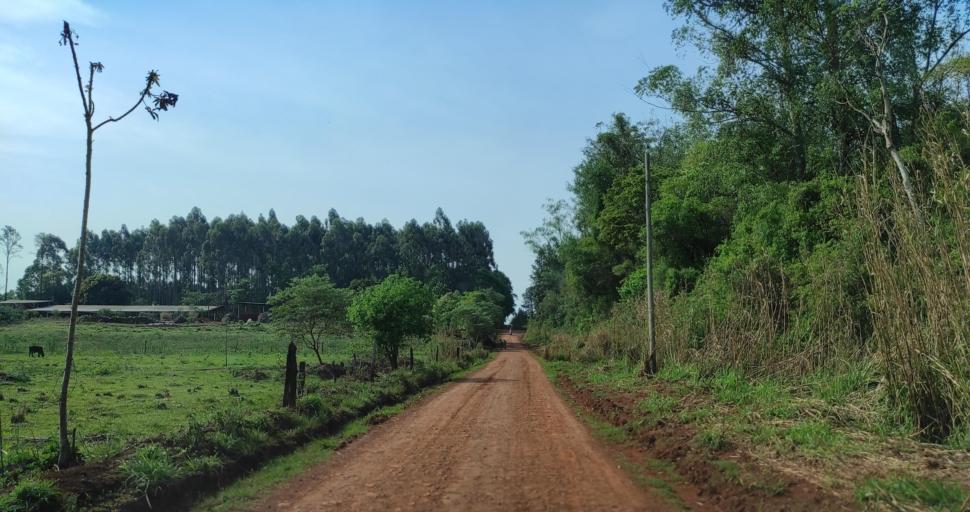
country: AR
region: Misiones
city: Capiovi
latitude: -26.8819
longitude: -55.0481
